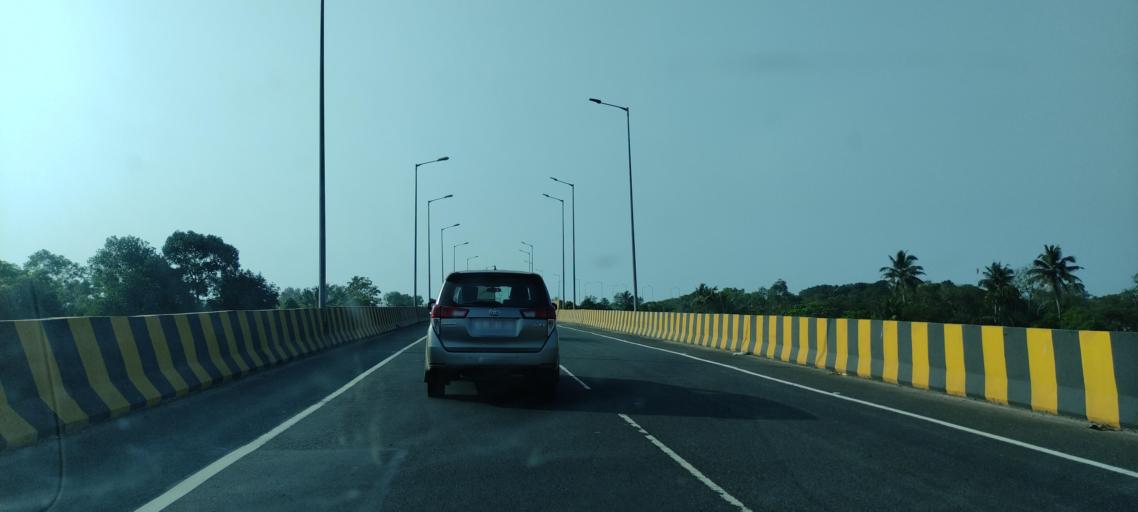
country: IN
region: Kerala
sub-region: Alappuzha
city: Alleppey
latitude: 9.4769
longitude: 76.3247
